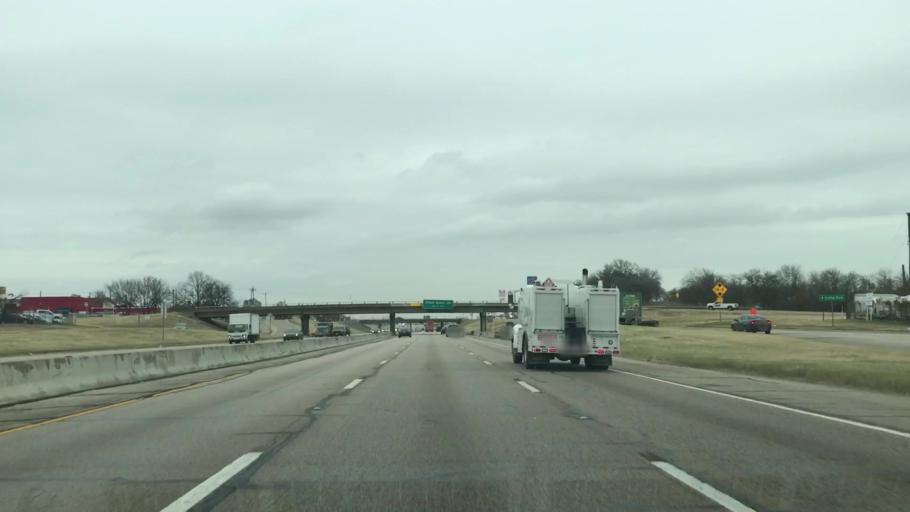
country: US
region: Texas
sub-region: Dallas County
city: Irving
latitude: 32.8051
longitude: -96.9216
